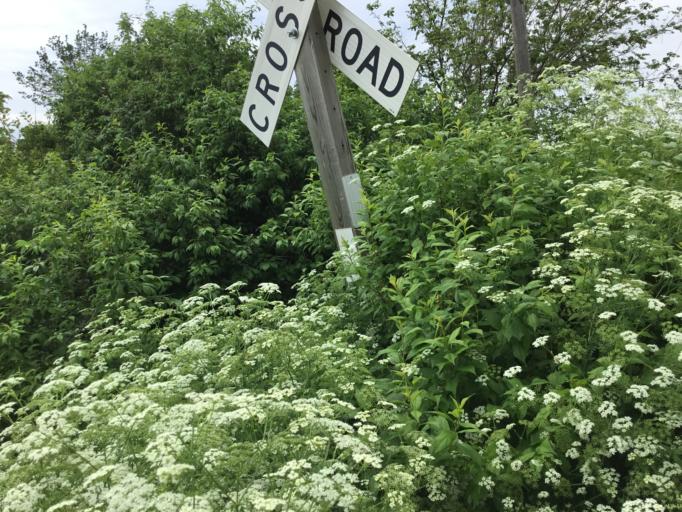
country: US
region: Kansas
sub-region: Republic County
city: Belleville
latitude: 39.8557
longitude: -97.5845
